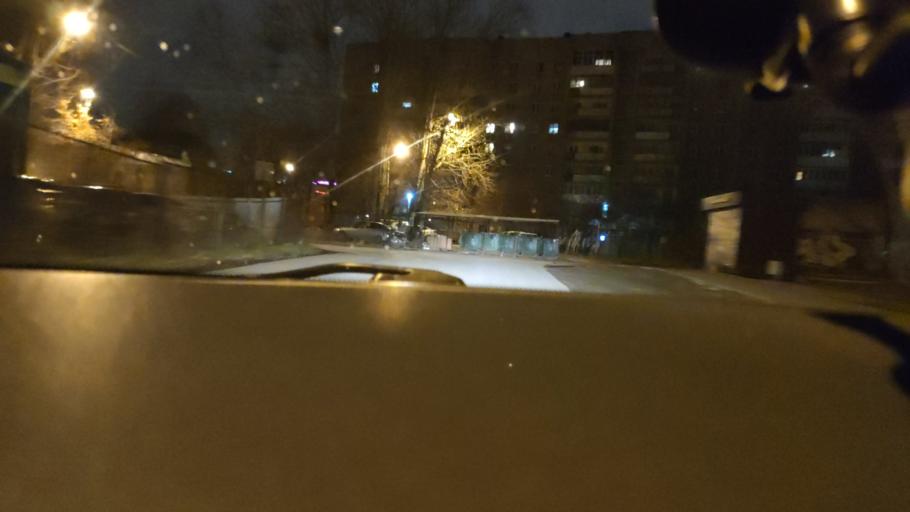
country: RU
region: Perm
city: Perm
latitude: 58.0114
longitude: 56.2962
